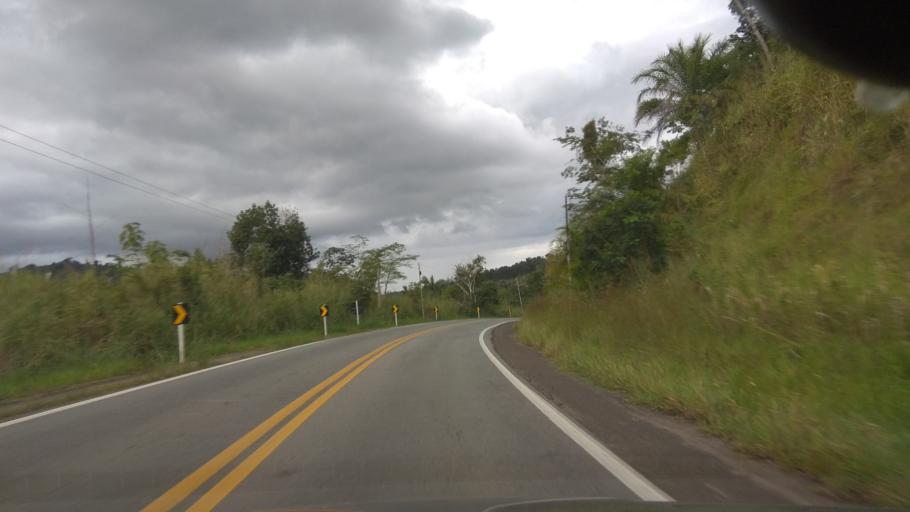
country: BR
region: Bahia
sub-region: Ubata
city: Ubata
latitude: -14.1930
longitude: -39.5590
